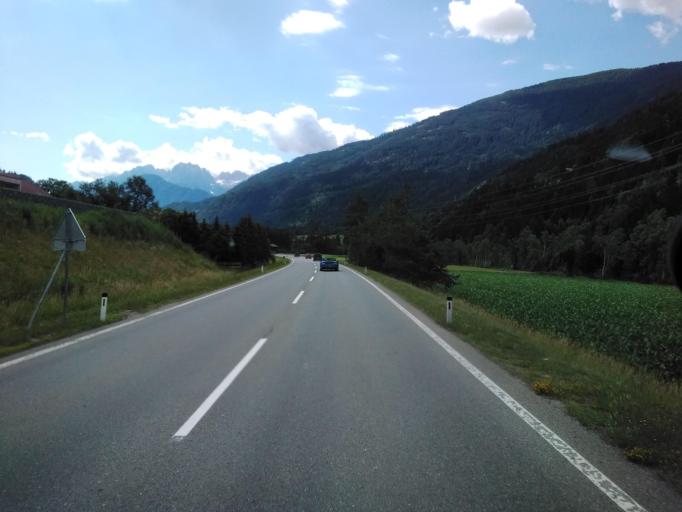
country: AT
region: Tyrol
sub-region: Politischer Bezirk Lienz
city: Ainet
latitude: 46.8630
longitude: 12.6887
